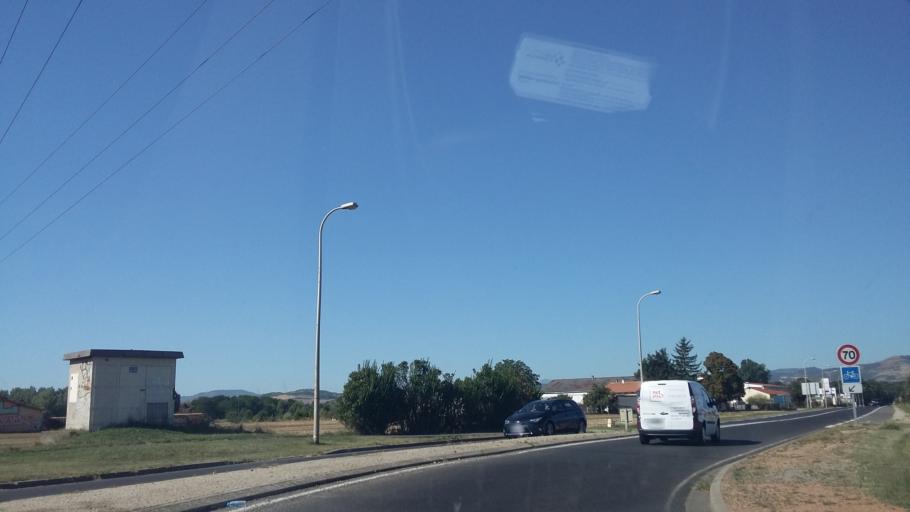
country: FR
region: Auvergne
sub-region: Departement du Puy-de-Dome
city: Perignat-sur-Allier
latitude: 45.7301
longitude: 3.2276
